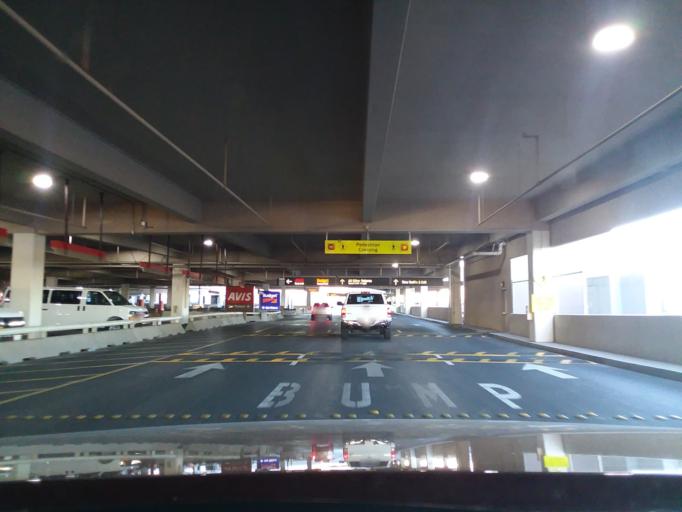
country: US
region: Nevada
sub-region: Clark County
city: Paradise
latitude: 36.0614
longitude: -115.1650
